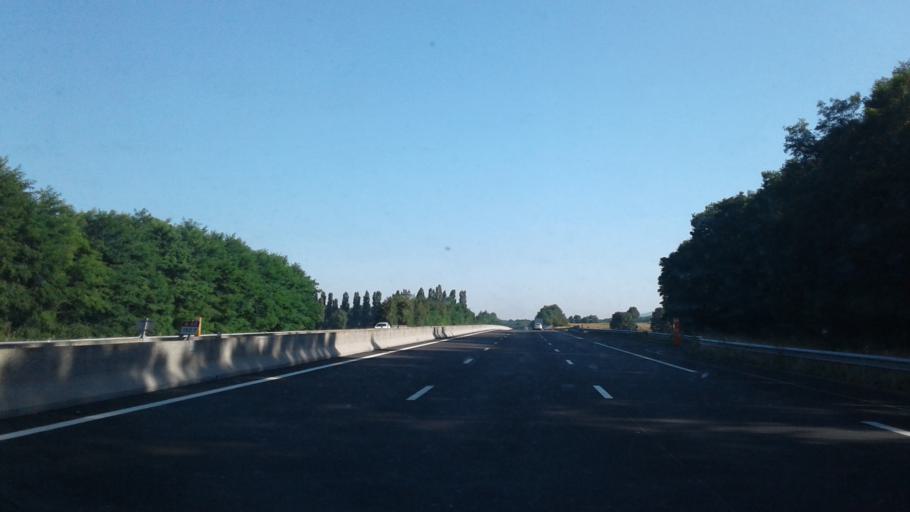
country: FR
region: Rhone-Alpes
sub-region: Departement de l'Ain
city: Saint-Martin-du-Mont
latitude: 46.0964
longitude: 5.2895
